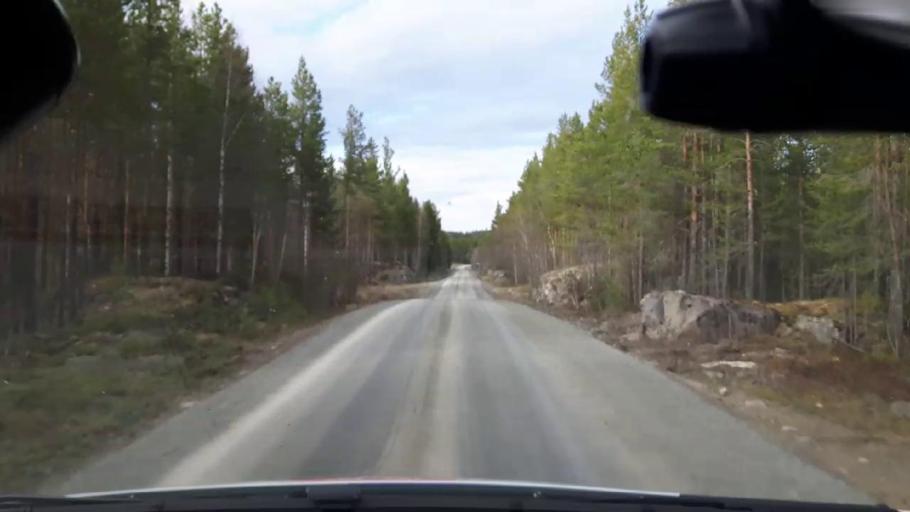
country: SE
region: Jaemtland
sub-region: Bergs Kommun
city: Hoverberg
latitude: 62.9296
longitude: 14.6473
